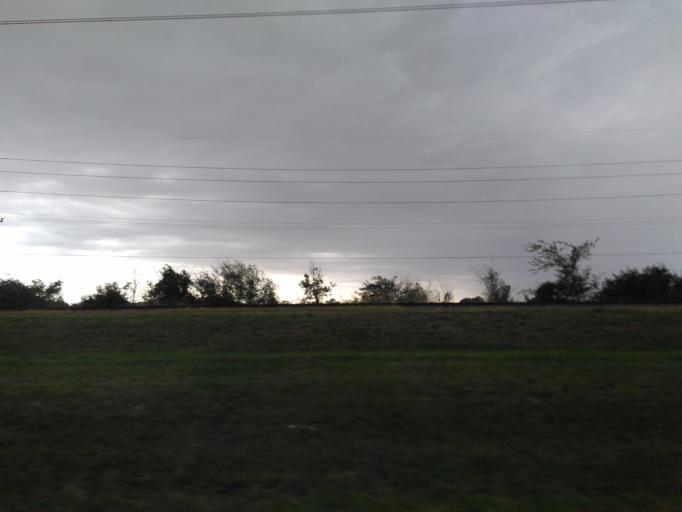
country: US
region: Illinois
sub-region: Madison County
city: Saint Jacob
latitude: 38.7188
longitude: -89.7772
